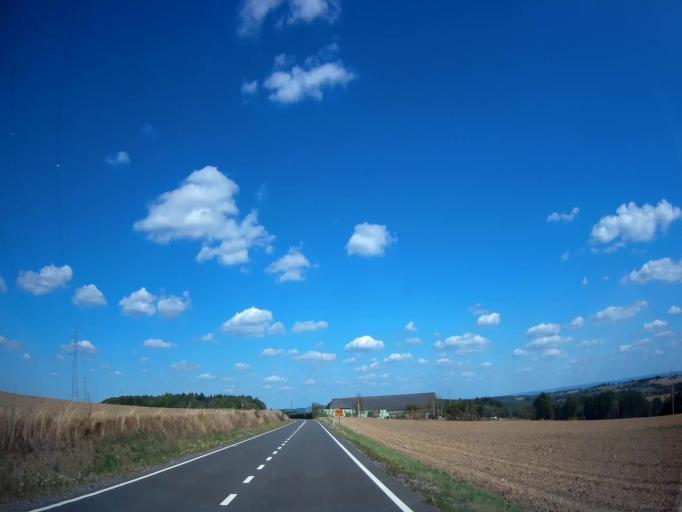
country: BE
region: Wallonia
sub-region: Province de Namur
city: Beauraing
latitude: 50.1785
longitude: 4.9200
